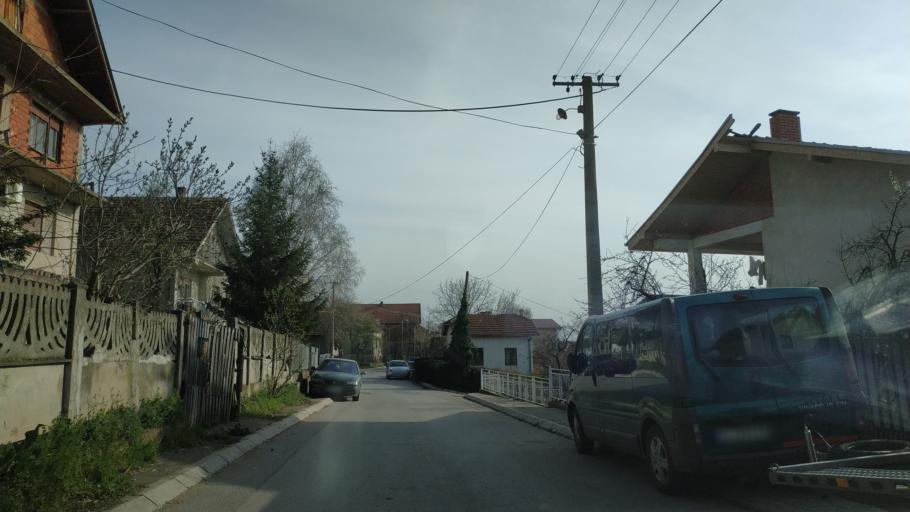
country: RS
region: Central Serbia
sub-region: Nisavski Okrug
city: Aleksinac
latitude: 43.5432
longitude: 21.7169
